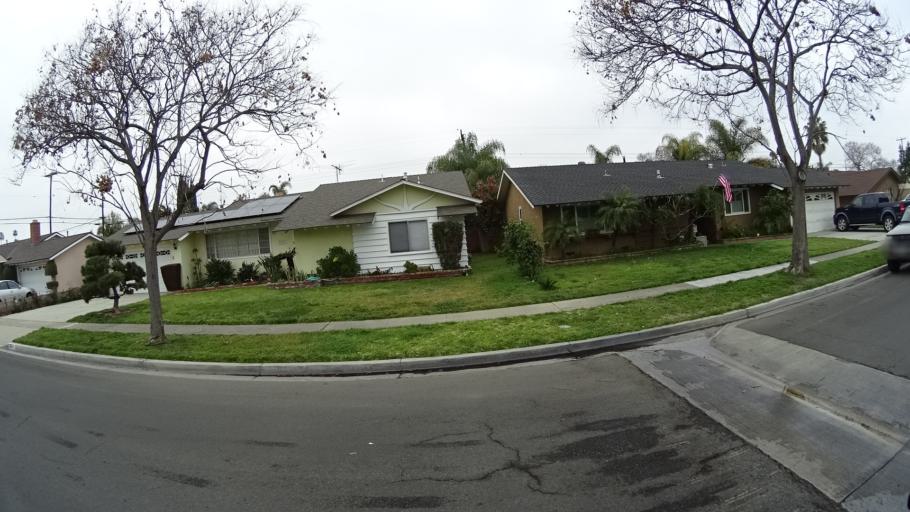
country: US
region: California
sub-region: Orange County
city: Stanton
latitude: 33.8215
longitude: -118.0082
